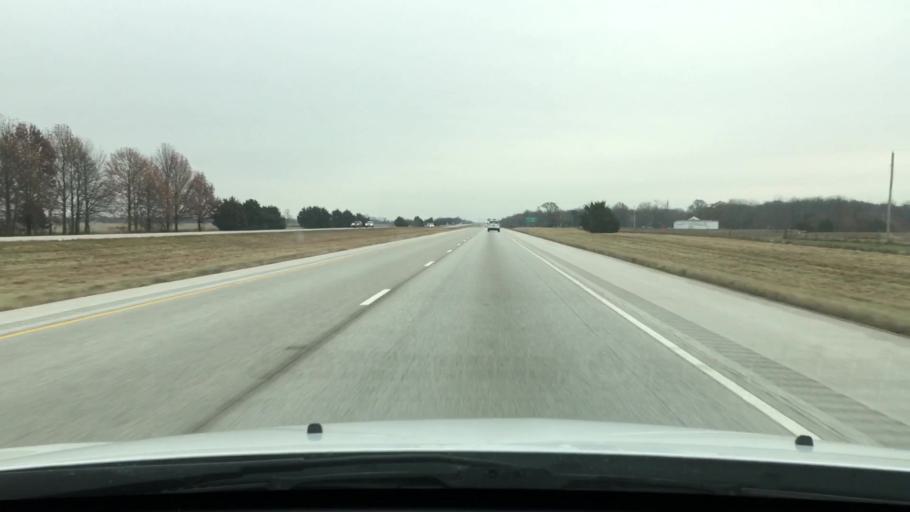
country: US
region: Illinois
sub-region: Morgan County
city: South Jacksonville
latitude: 39.6802
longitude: -90.3178
